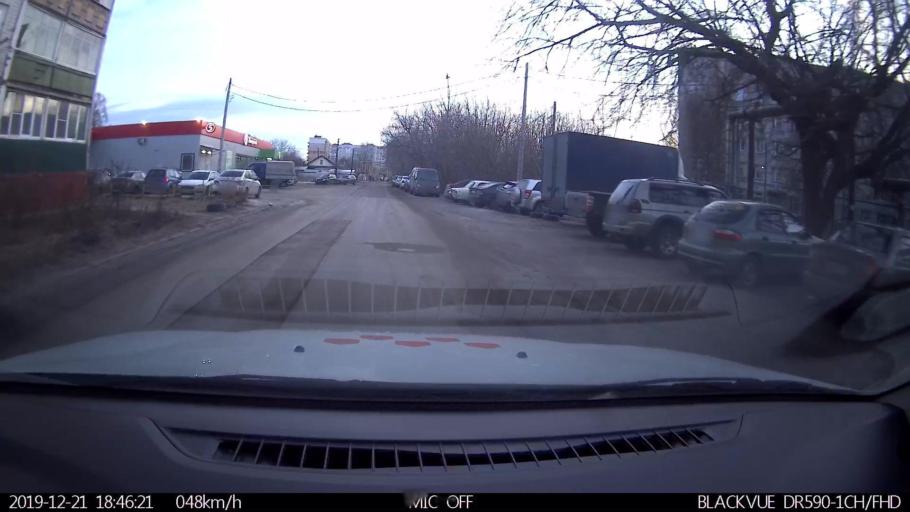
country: RU
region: Nizjnij Novgorod
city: Nizhniy Novgorod
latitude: 56.3292
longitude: 43.9231
